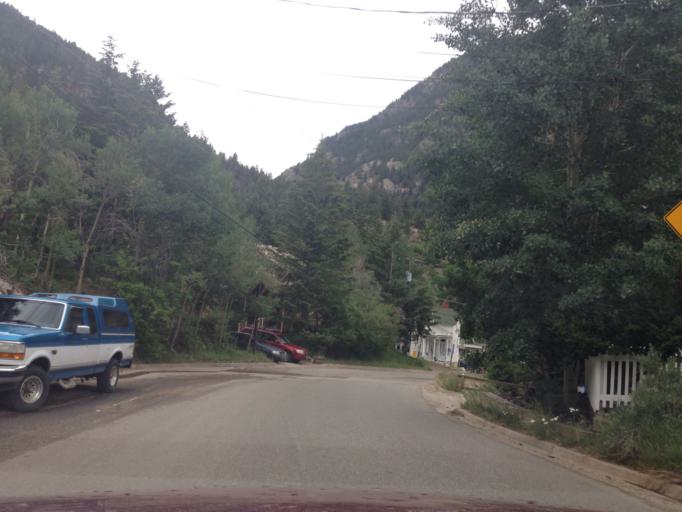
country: US
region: Colorado
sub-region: Clear Creek County
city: Georgetown
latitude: 39.7036
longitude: -105.6973
